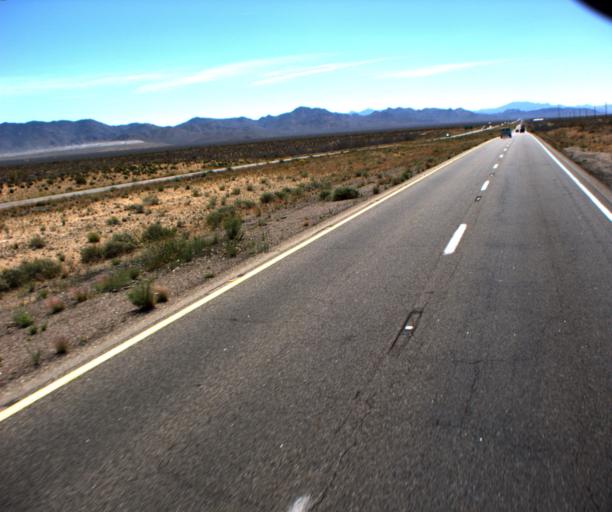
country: US
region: Arizona
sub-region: Mohave County
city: Golden Valley
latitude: 35.3575
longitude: -114.2311
